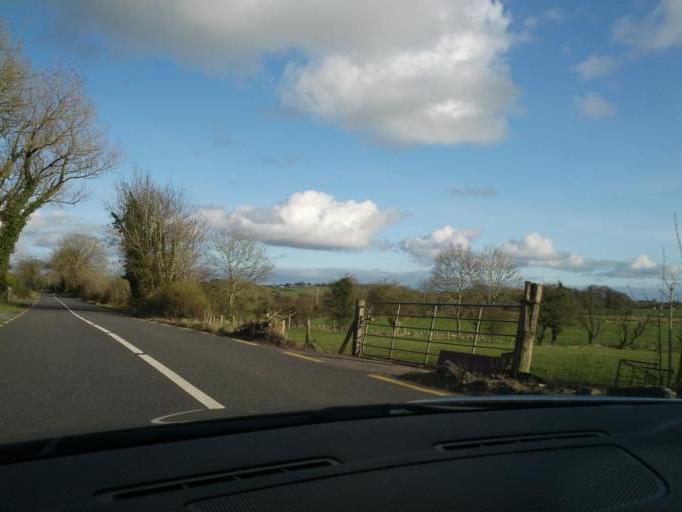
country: IE
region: Connaught
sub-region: Roscommon
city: Roscommon
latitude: 53.6627
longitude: -8.2869
